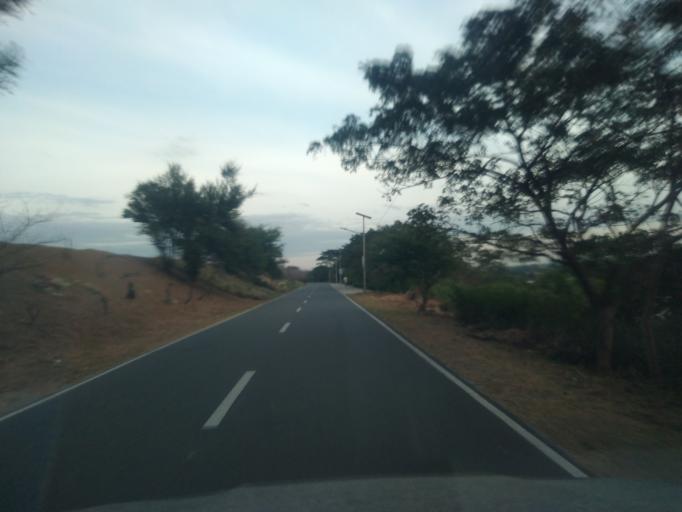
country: PH
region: Central Luzon
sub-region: Province of Pampanga
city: Santa Rita
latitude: 15.0177
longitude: 120.6094
